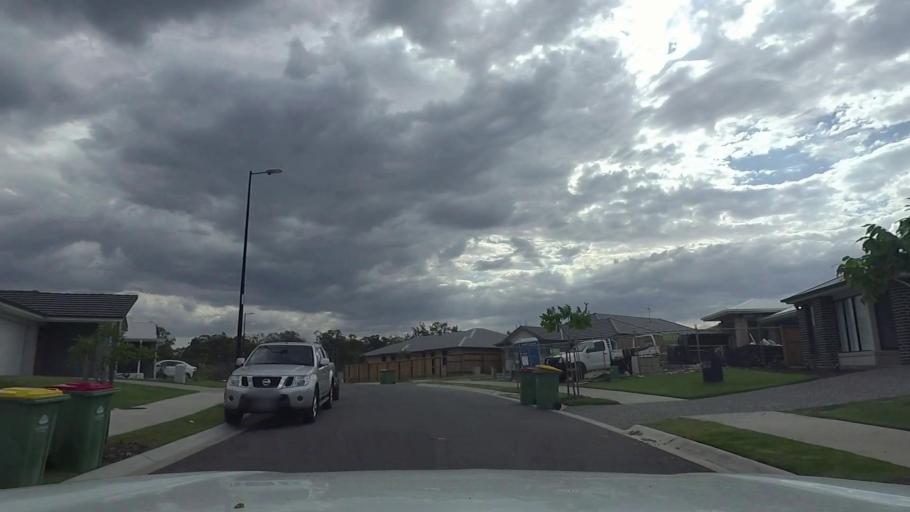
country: AU
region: Queensland
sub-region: Logan
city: Windaroo
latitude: -27.7332
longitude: 153.1657
